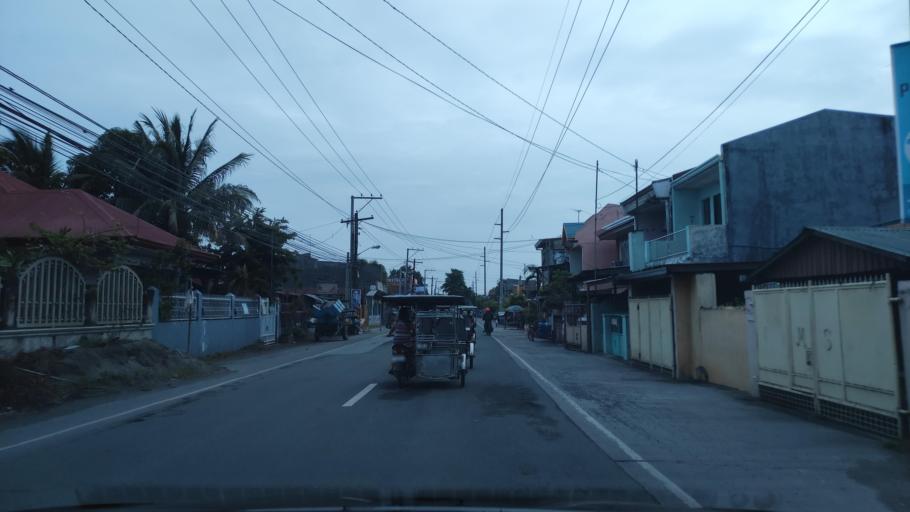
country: PH
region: Central Luzon
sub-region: Province of Pampanga
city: Santa Ana
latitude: 15.1092
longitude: 120.7719
